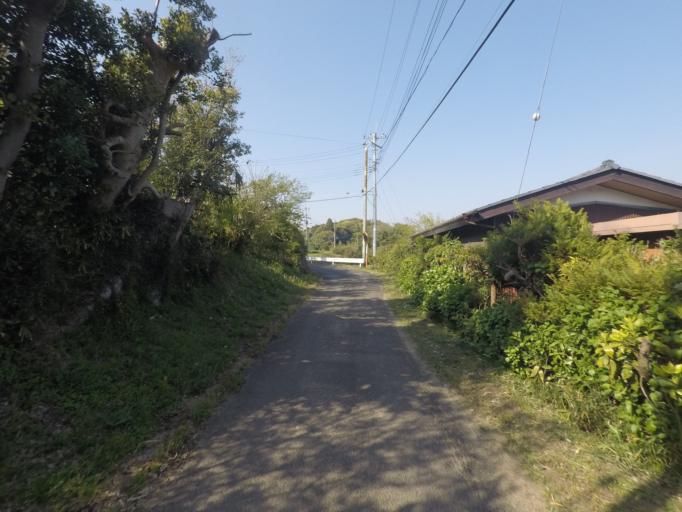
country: JP
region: Ibaraki
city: Inashiki
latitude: 36.0604
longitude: 140.4411
